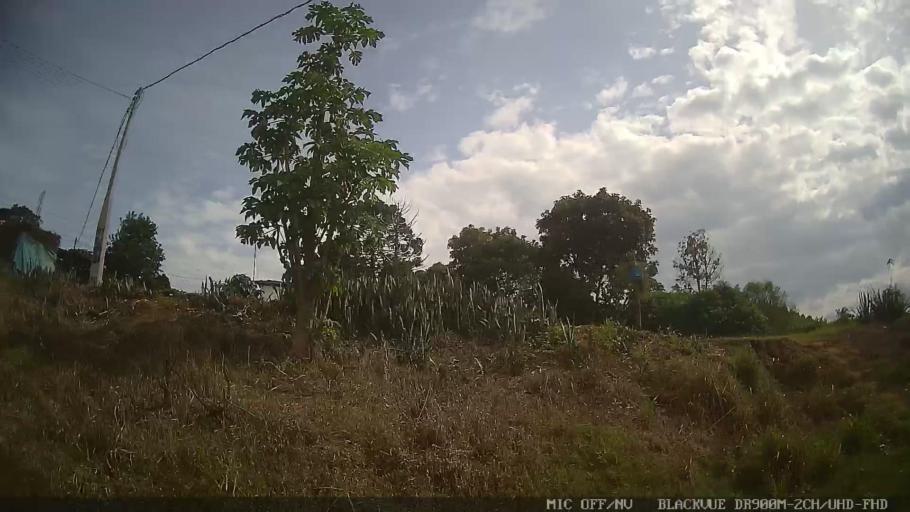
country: BR
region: Sao Paulo
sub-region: Mogi das Cruzes
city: Mogi das Cruzes
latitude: -23.6502
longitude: -46.2244
